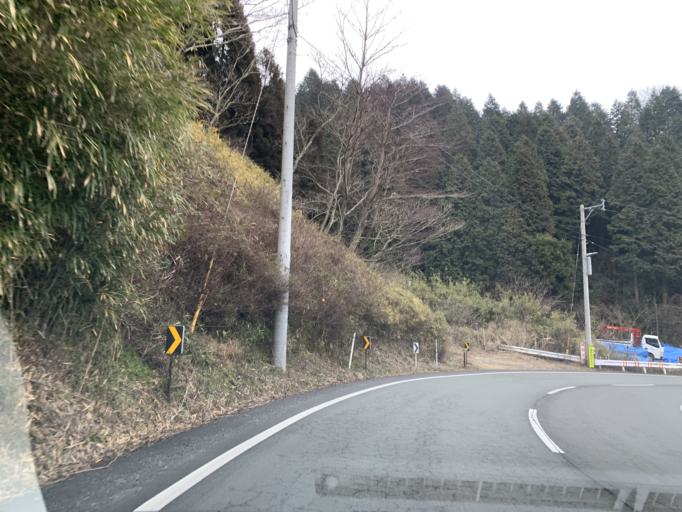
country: JP
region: Kumamoto
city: Aso
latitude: 32.9182
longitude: 130.9701
